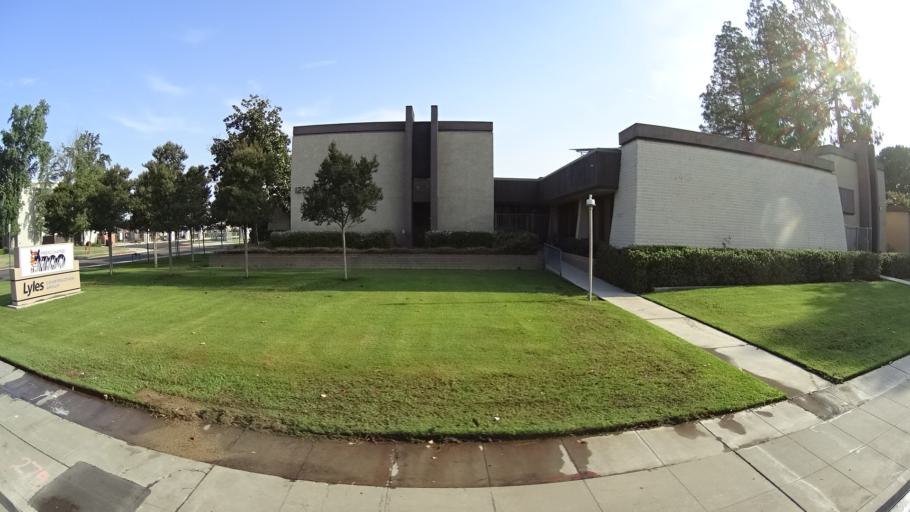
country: US
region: California
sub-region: Fresno County
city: West Park
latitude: 36.7575
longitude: -119.8262
